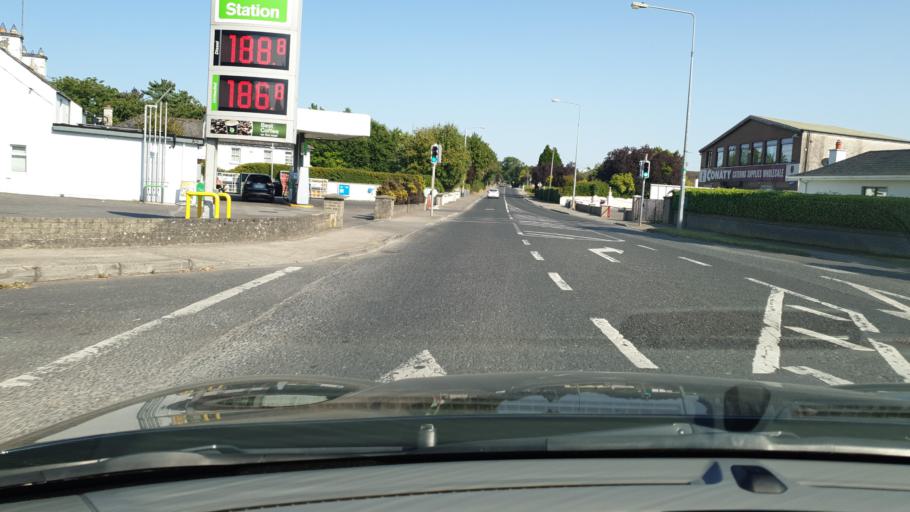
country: IE
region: Leinster
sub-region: An Mhi
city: Navan
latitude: 53.6507
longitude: -6.6649
